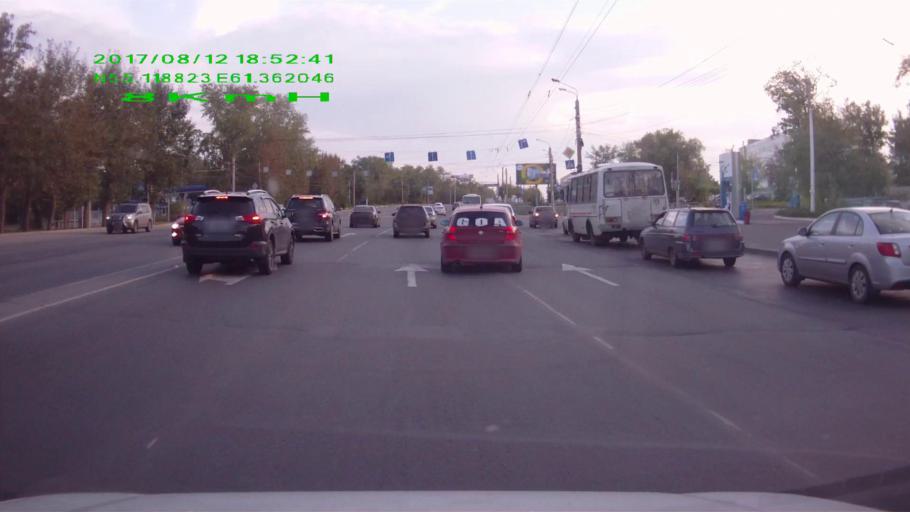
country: RU
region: Chelyabinsk
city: Novosineglazovskiy
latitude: 55.1143
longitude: 61.3589
